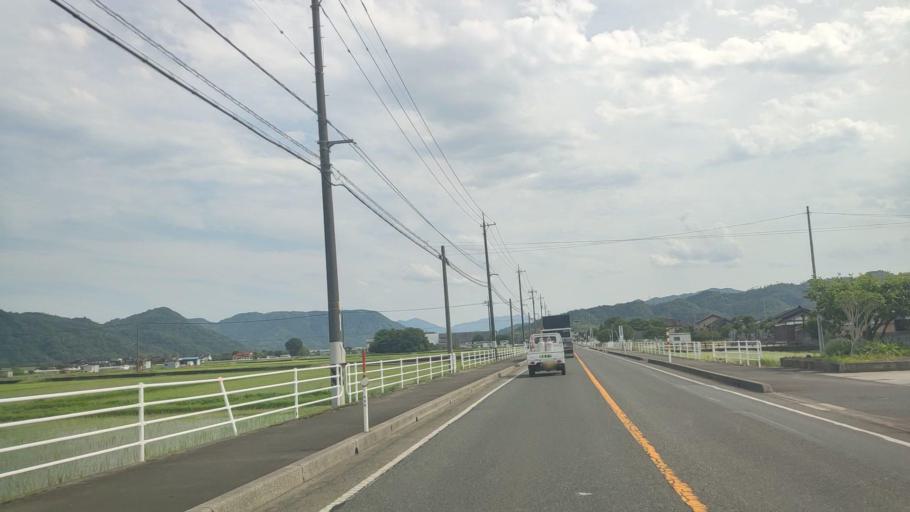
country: JP
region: Tottori
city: Tottori
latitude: 35.4600
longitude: 134.2038
